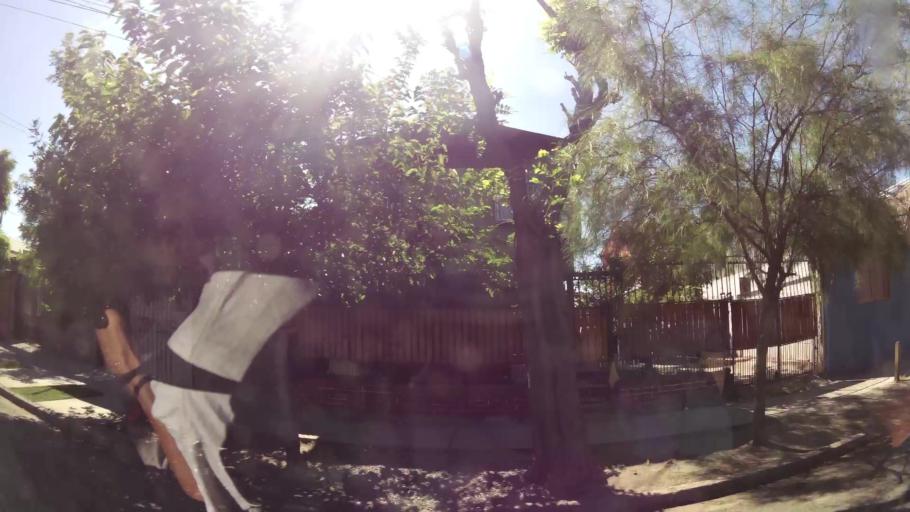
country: CL
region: Santiago Metropolitan
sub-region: Provincia de Santiago
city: La Pintana
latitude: -33.5563
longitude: -70.6613
